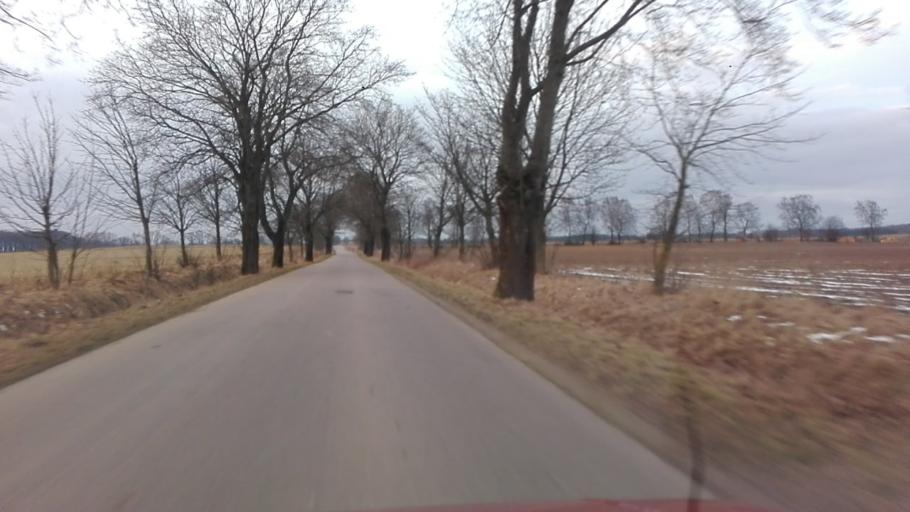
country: PL
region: West Pomeranian Voivodeship
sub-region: Powiat swidwinski
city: Rabino
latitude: 53.8126
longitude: 15.9210
